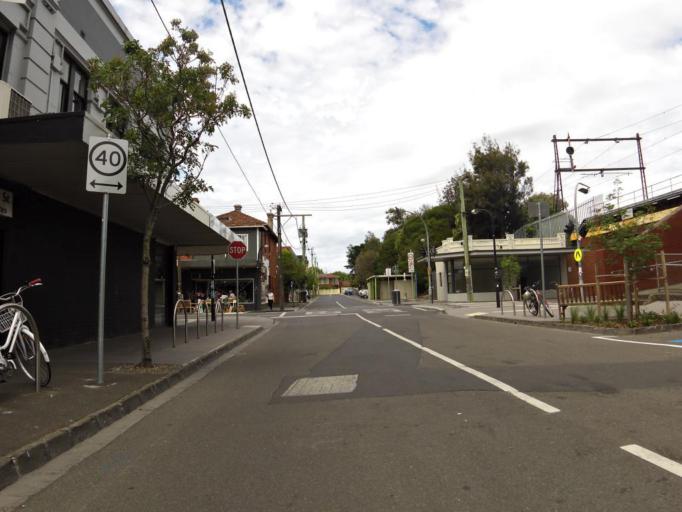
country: AU
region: Victoria
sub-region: Bayside
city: North Brighton
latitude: -37.8972
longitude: 145.0043
